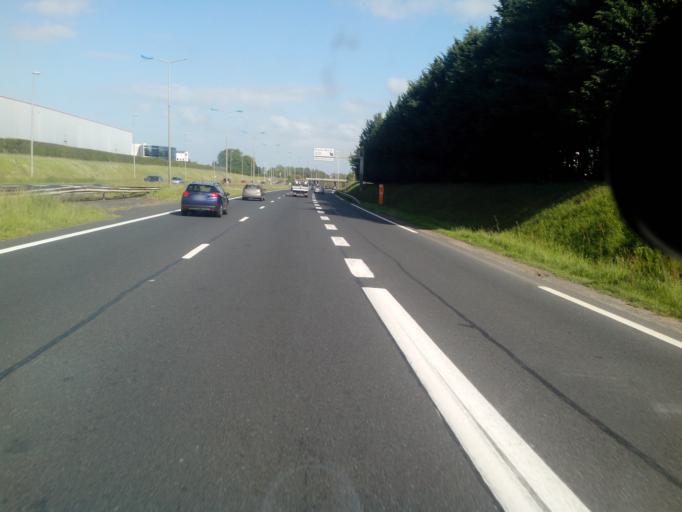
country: FR
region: Lower Normandy
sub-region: Departement du Calvados
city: Caen
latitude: 49.2016
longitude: -0.3508
